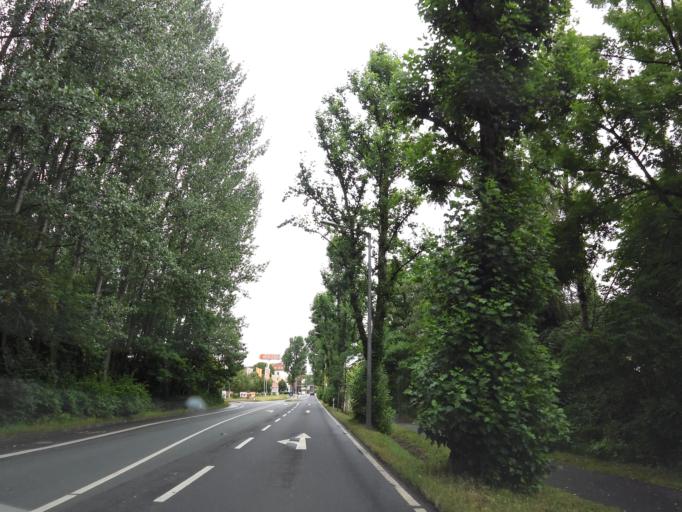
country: DE
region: Saxony
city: Markkleeberg
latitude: 51.3006
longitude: 12.4268
